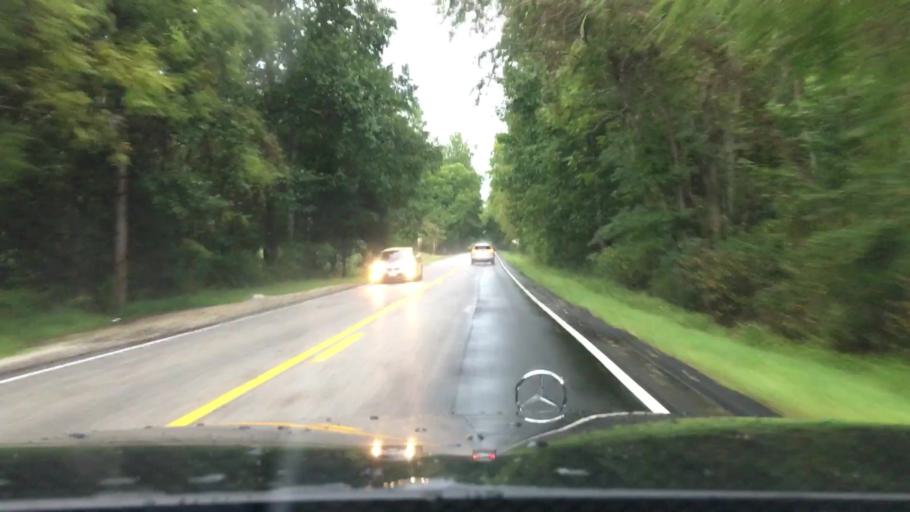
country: US
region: Virginia
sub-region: Amherst County
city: Amherst
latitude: 37.6725
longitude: -79.0140
